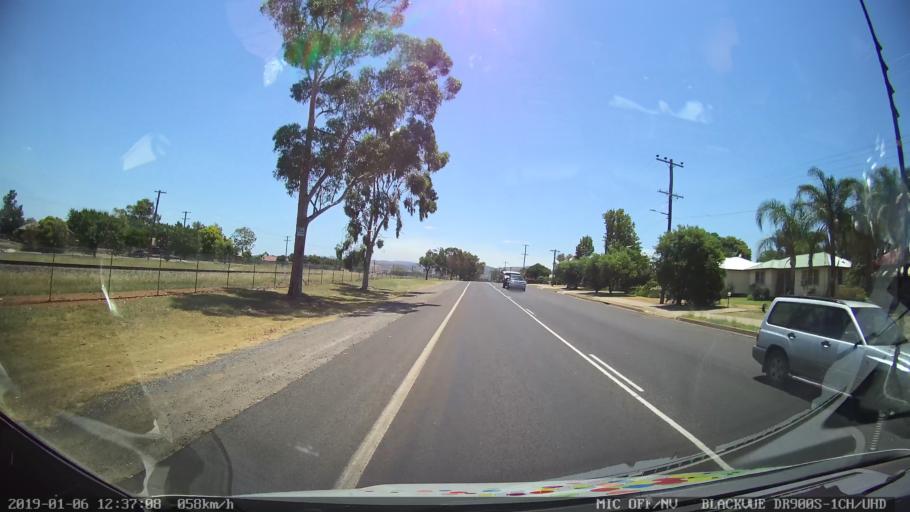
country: AU
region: New South Wales
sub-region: Tamworth Municipality
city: South Tamworth
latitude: -31.1067
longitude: 150.9002
